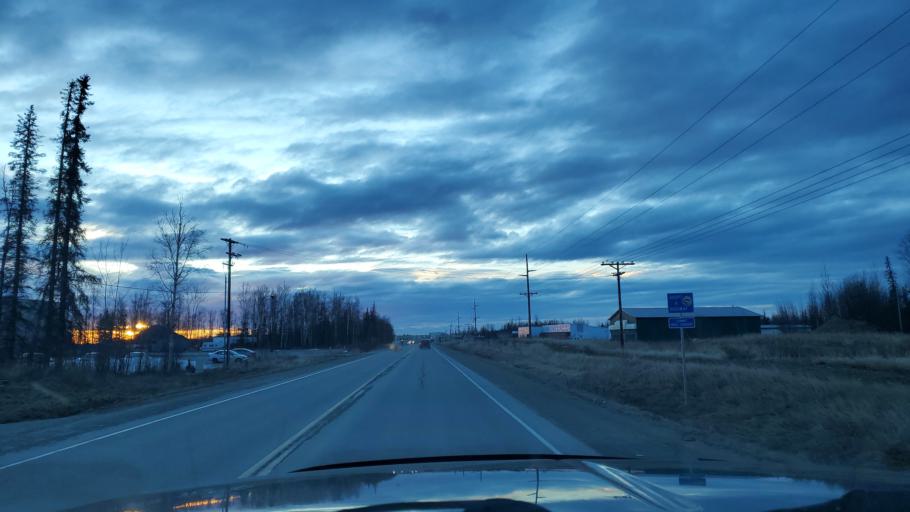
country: US
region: Alaska
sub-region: Matanuska-Susitna Borough
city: Wasilla
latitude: 61.5923
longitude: -149.3946
